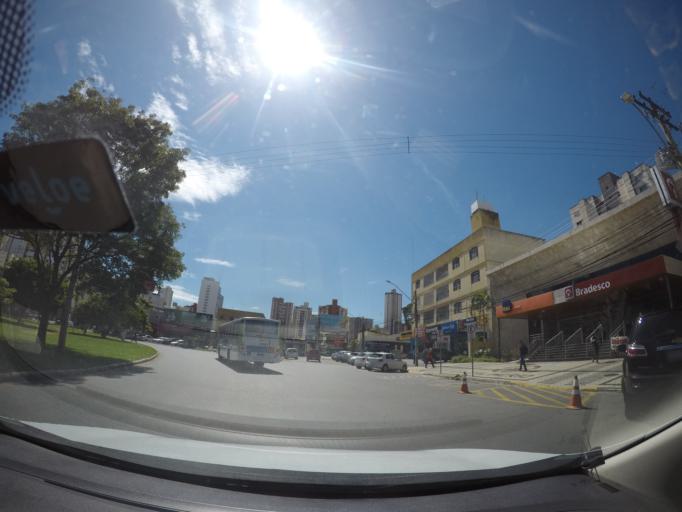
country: BR
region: Goias
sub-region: Goiania
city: Goiania
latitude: -16.7148
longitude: -49.2740
